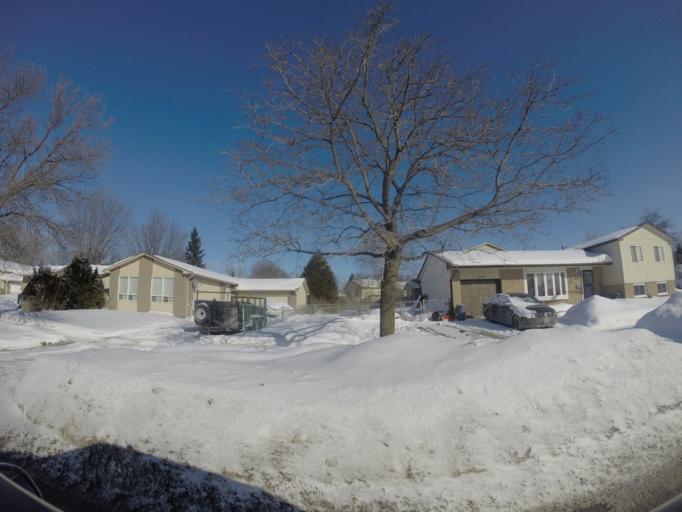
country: CA
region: Ontario
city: Barrie
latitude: 44.3934
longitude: -79.7227
